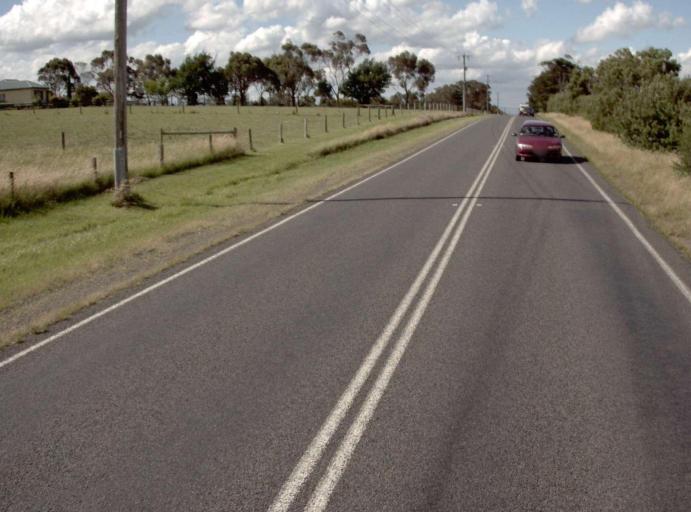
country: AU
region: Victoria
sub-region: Latrobe
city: Morwell
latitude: -38.2877
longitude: 146.4302
